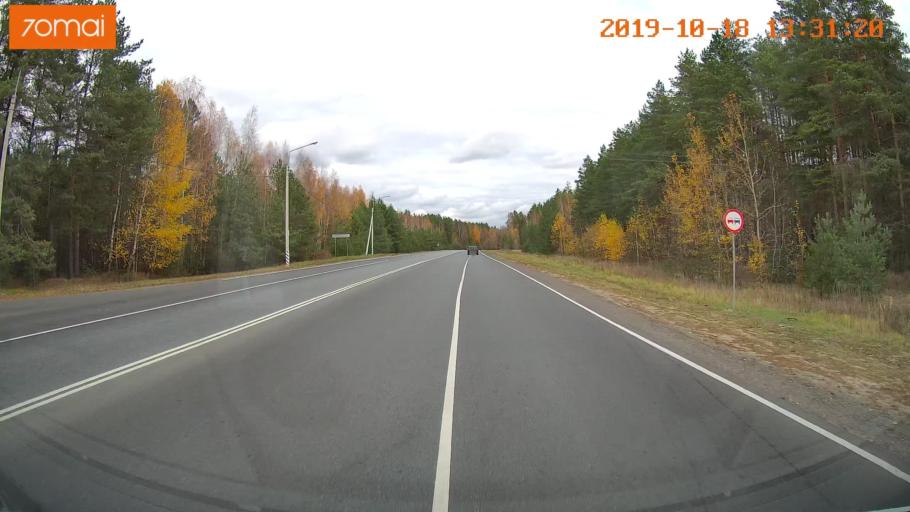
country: RU
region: Rjazan
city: Solotcha
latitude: 54.8211
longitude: 39.8982
